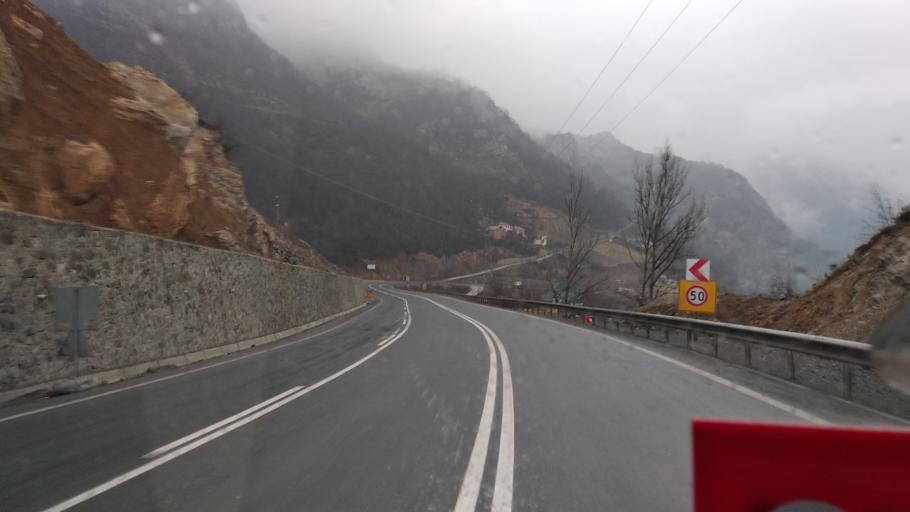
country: TR
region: Trabzon
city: Macka
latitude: 40.7150
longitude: 39.5148
